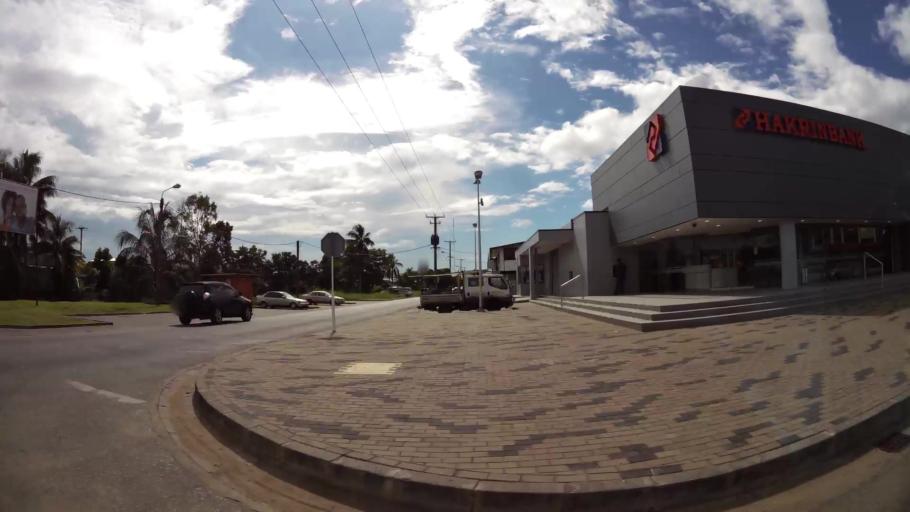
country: SR
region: Paramaribo
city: Paramaribo
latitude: 5.8457
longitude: -55.1479
